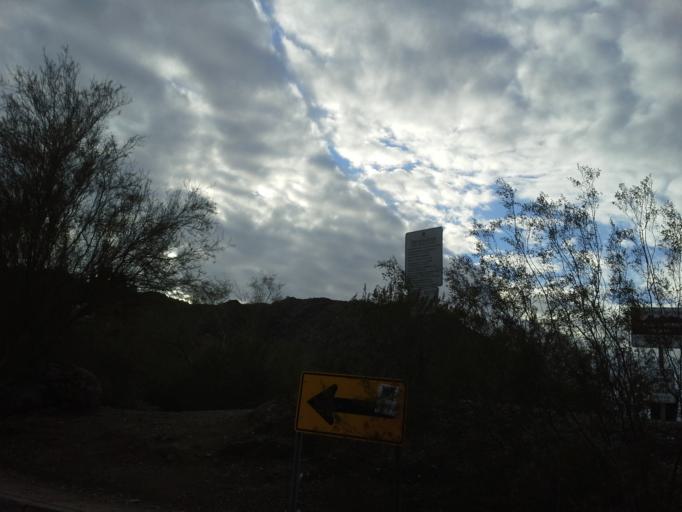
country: US
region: Arizona
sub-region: Maricopa County
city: Paradise Valley
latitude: 33.5844
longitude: -112.0370
